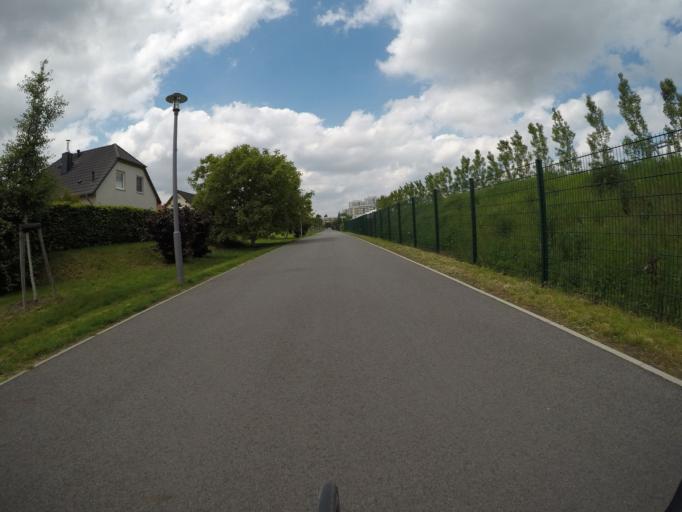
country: DE
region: Berlin
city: Marzahn
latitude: 52.5345
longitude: 13.5709
